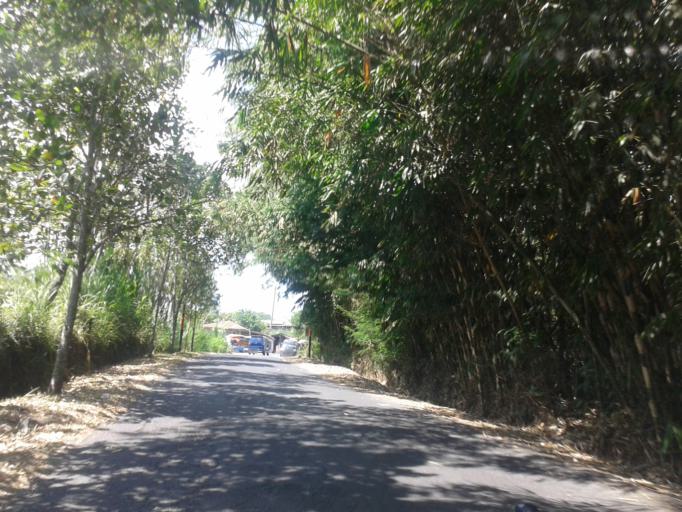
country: ID
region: Bali
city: Banjar Kedisan
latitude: -8.2864
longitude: 115.3471
